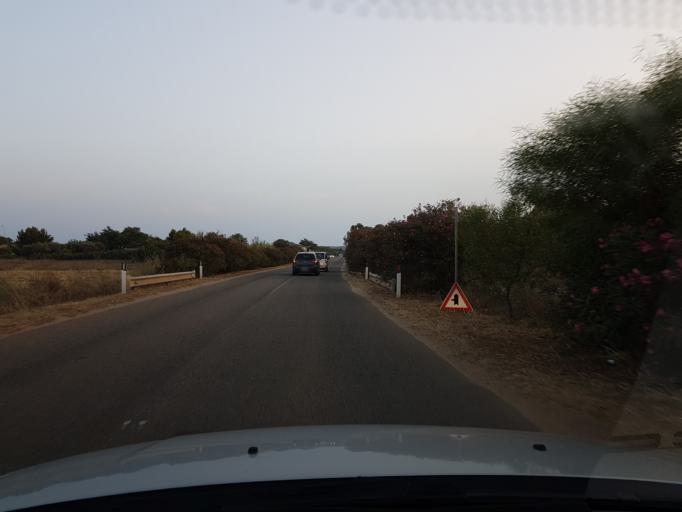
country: IT
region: Sardinia
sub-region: Provincia di Oristano
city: Cabras
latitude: 39.9231
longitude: 8.4526
